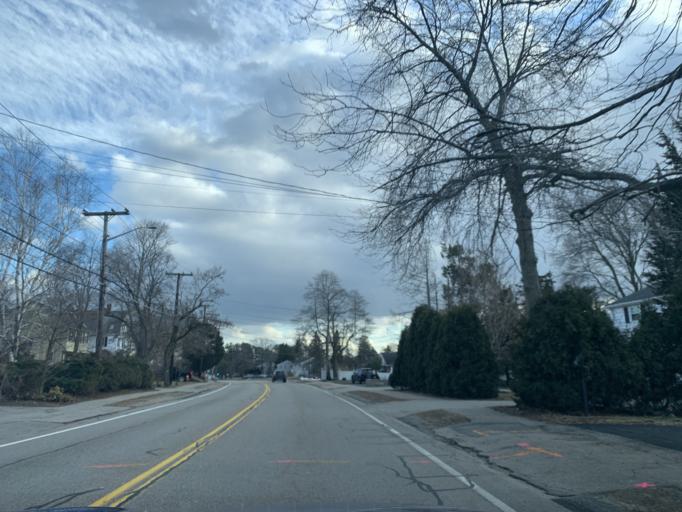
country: US
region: Massachusetts
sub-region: Norfolk County
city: Norwood
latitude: 42.1796
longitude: -71.1810
